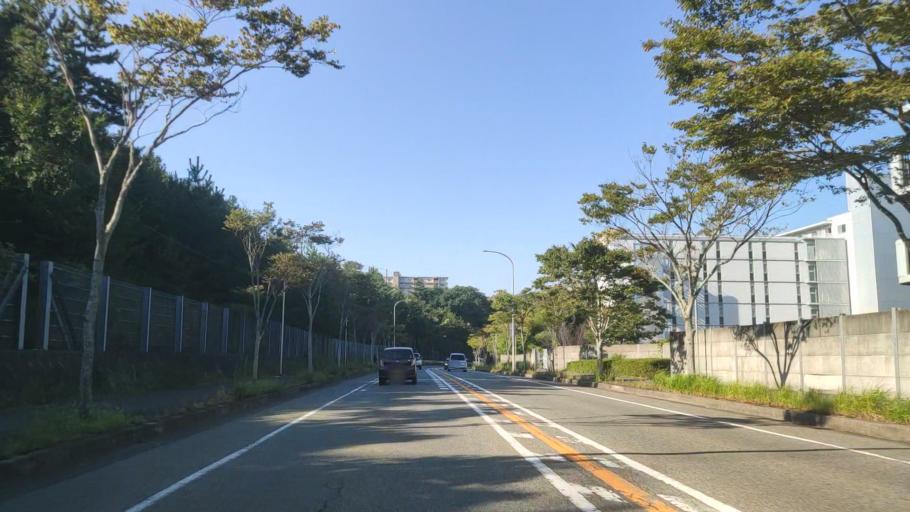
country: JP
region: Hyogo
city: Kobe
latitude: 34.7676
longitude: 135.1859
